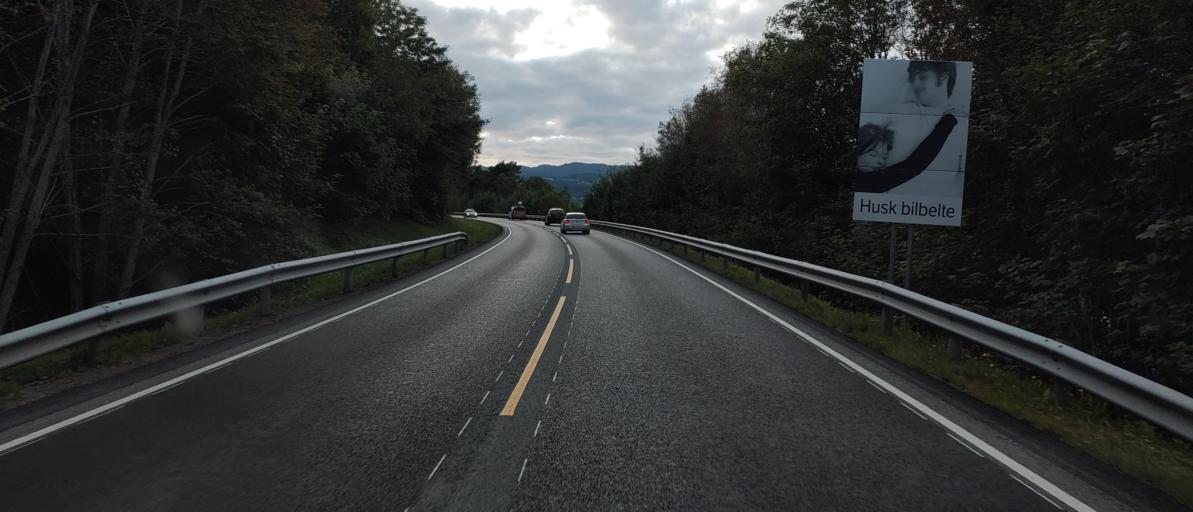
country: NO
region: More og Romsdal
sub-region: Molde
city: Molde
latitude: 62.7352
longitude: 7.3248
